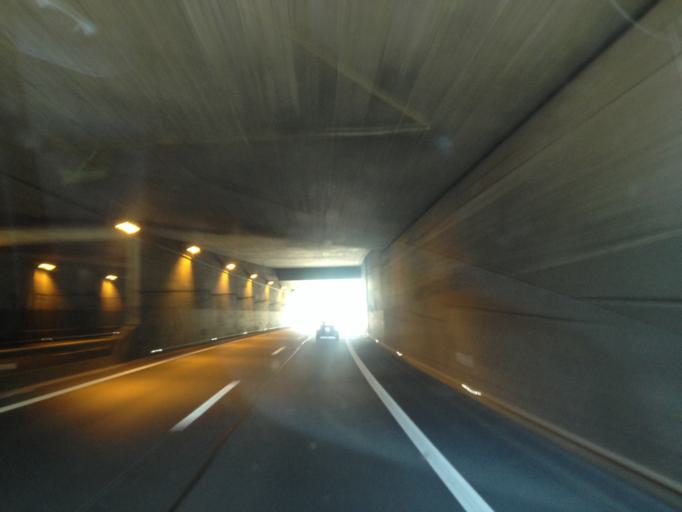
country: CH
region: Fribourg
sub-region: Sense District
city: Flamatt
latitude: 46.8952
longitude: 7.3509
